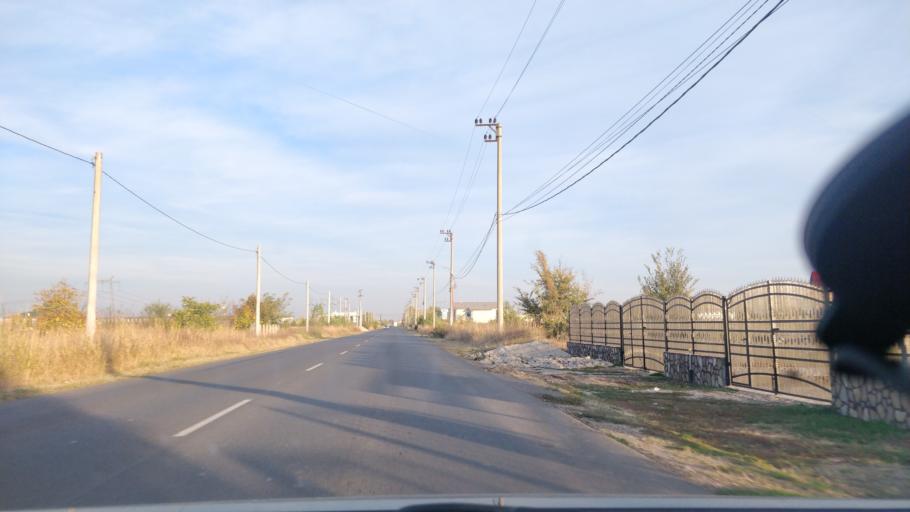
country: RO
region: Ilfov
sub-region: Comuna Ciorogarla
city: Ciorogarla
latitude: 44.4413
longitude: 25.9075
